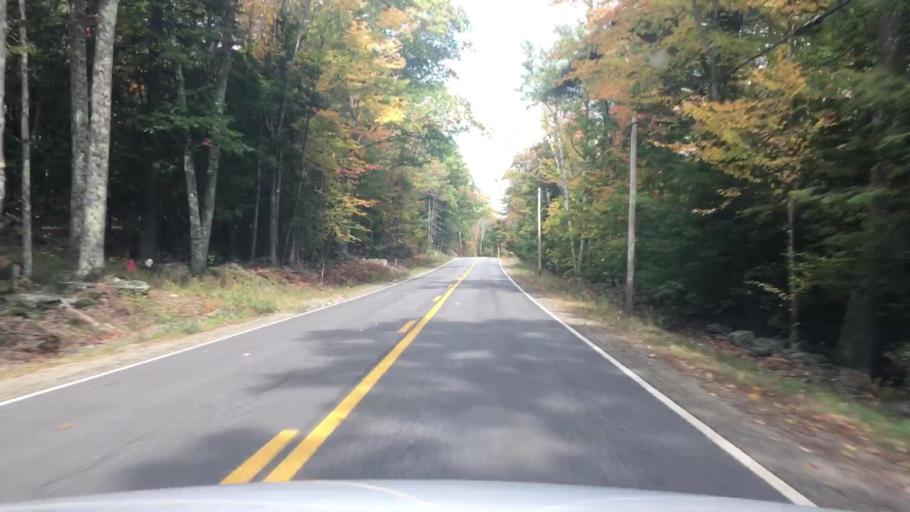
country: US
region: Maine
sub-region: Knox County
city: Hope
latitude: 44.2546
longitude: -69.1305
